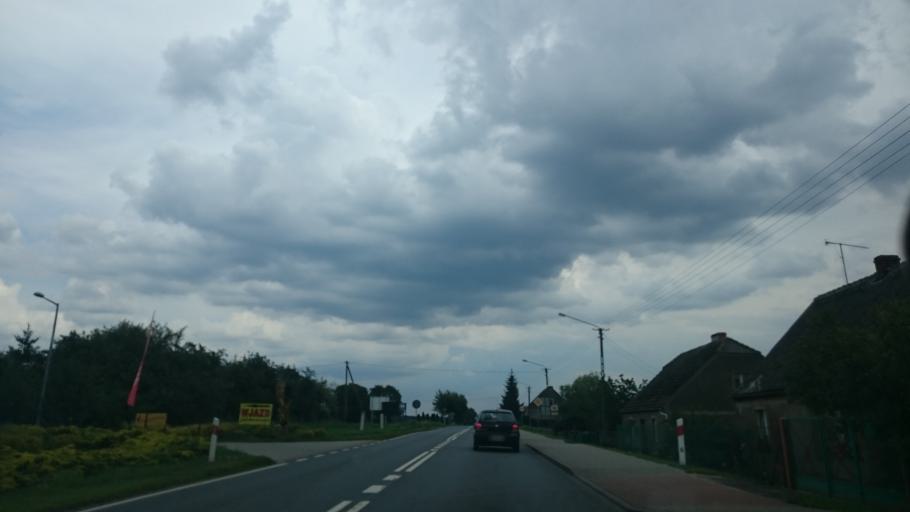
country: PL
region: Kujawsko-Pomorskie
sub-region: Powiat tucholski
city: Lubiewo
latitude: 53.5045
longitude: 18.0084
